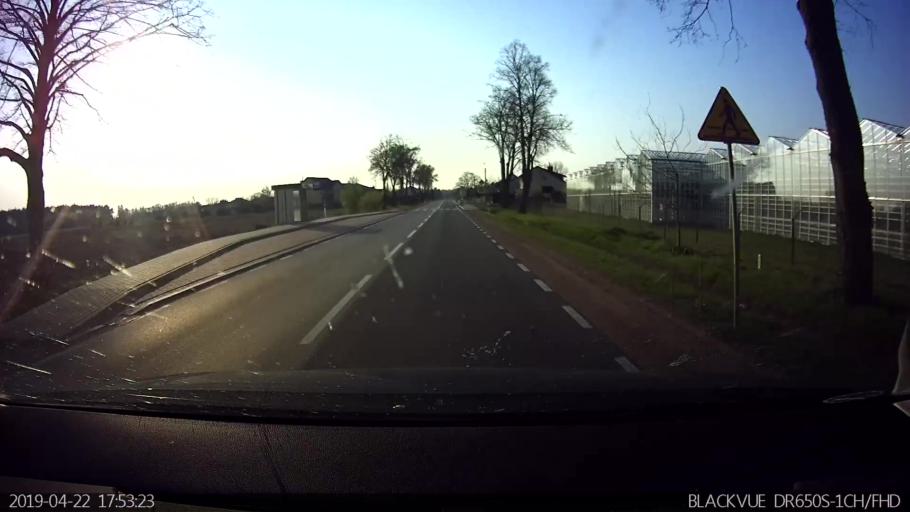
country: PL
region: Masovian Voivodeship
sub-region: Powiat wegrowski
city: Liw
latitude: 52.4525
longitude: 21.9554
